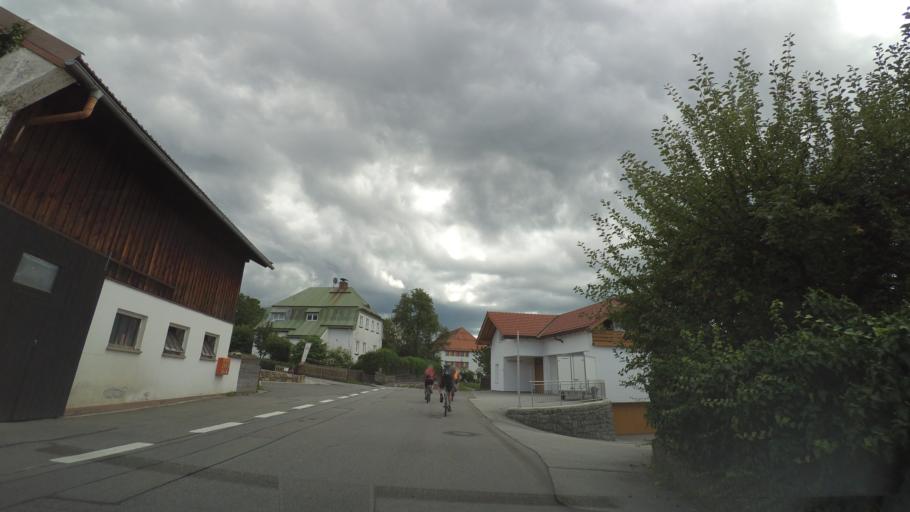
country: DE
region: Bavaria
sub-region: Lower Bavaria
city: Bodenmais
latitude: 49.0668
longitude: 13.0969
